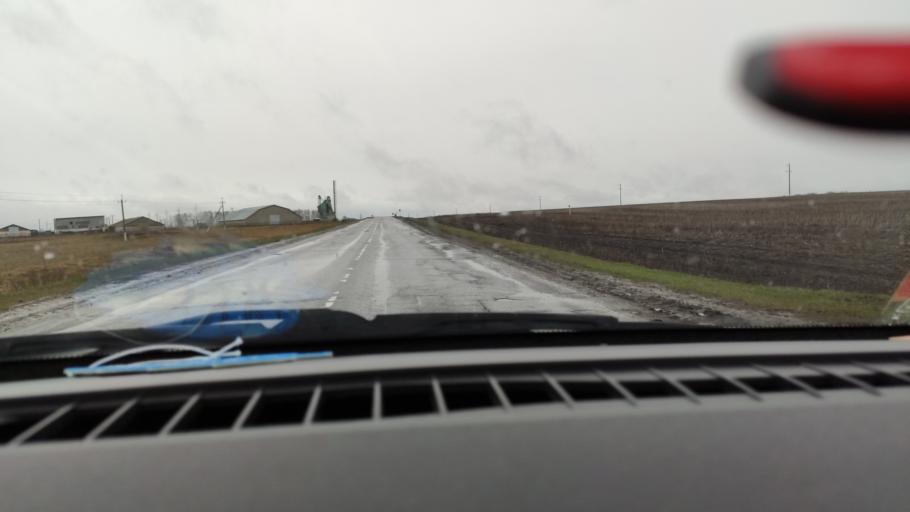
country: RU
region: Tatarstan
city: Nurlat
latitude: 54.6022
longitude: 50.8870
